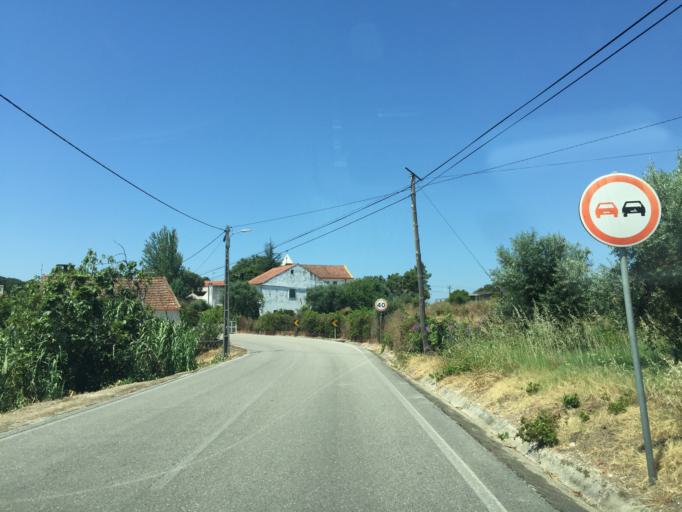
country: PT
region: Santarem
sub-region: Ferreira do Zezere
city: Ferreira do Zezere
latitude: 39.5952
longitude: -8.2731
